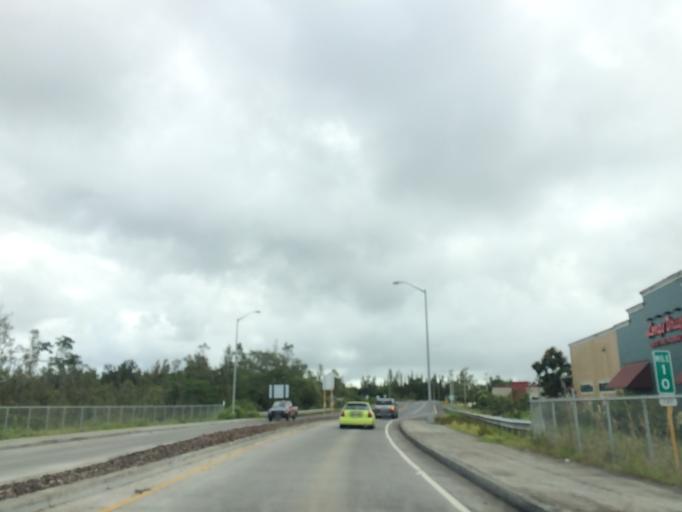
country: US
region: Hawaii
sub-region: Hawaii County
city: Hawaiian Paradise Park
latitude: 19.5052
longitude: -154.9558
